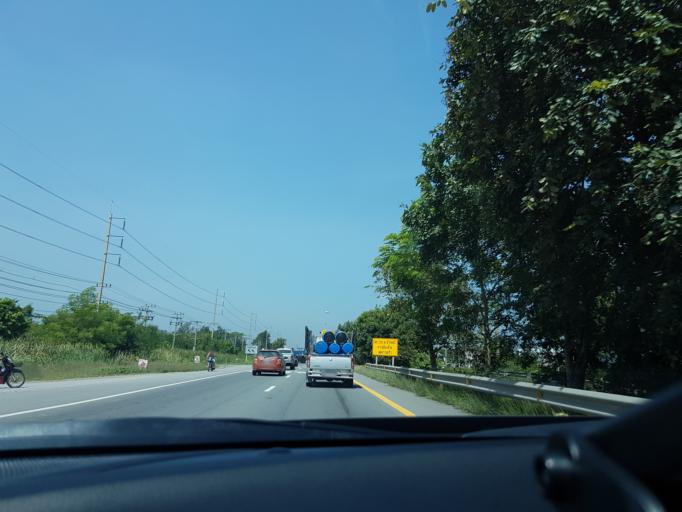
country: TH
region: Sara Buri
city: Saraburi
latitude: 14.5148
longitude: 100.8980
